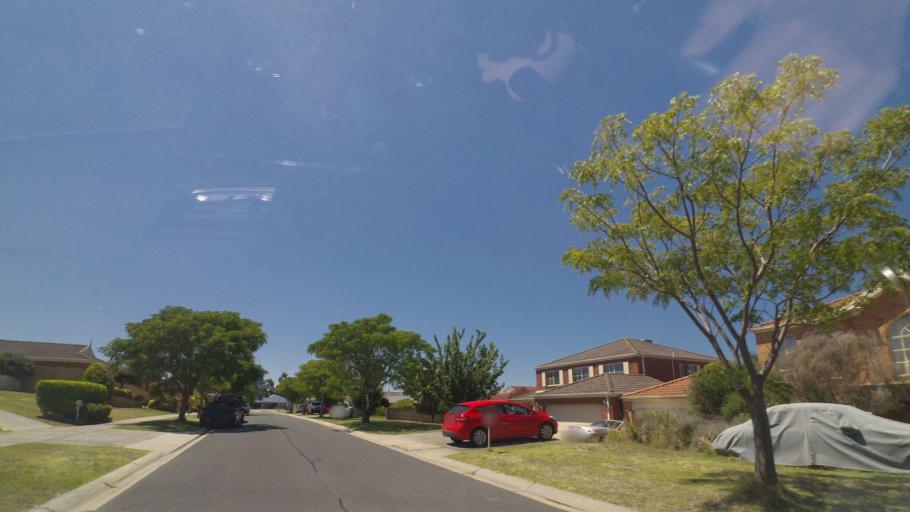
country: AU
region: Victoria
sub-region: Yarra Ranges
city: Lilydale
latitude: -37.7402
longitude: 145.3445
